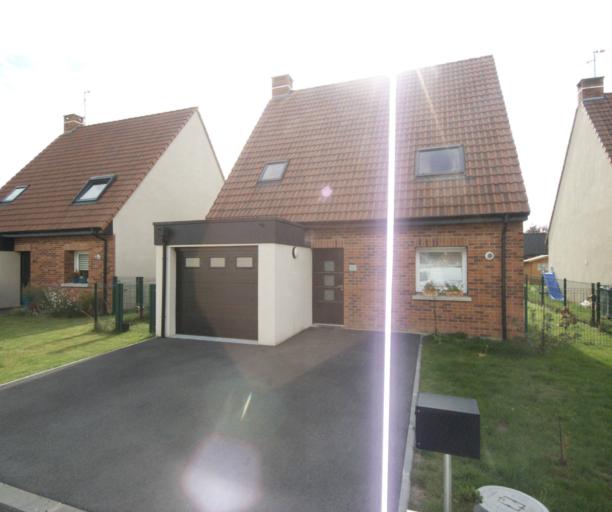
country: FR
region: Nord-Pas-de-Calais
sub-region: Departement du Nord
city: Herlies
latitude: 50.5813
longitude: 2.8611
